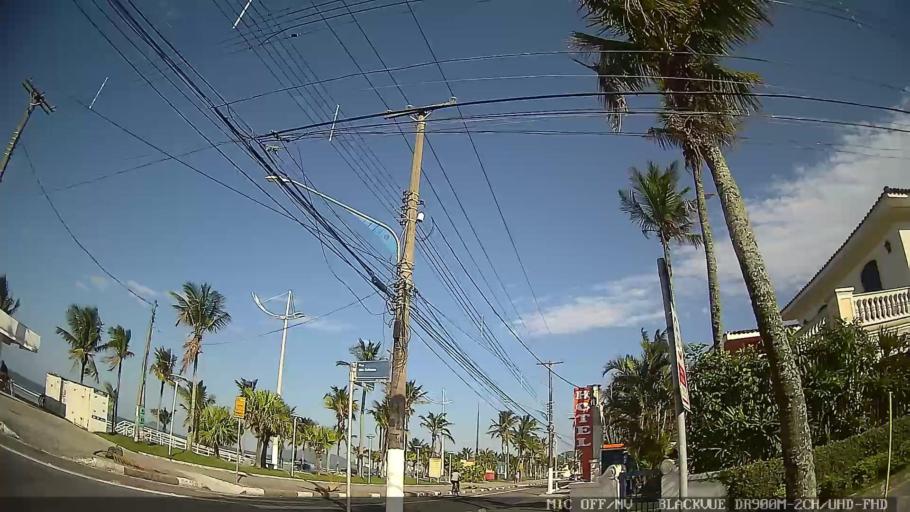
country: BR
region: Sao Paulo
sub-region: Guaruja
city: Guaruja
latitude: -23.9860
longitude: -46.2230
